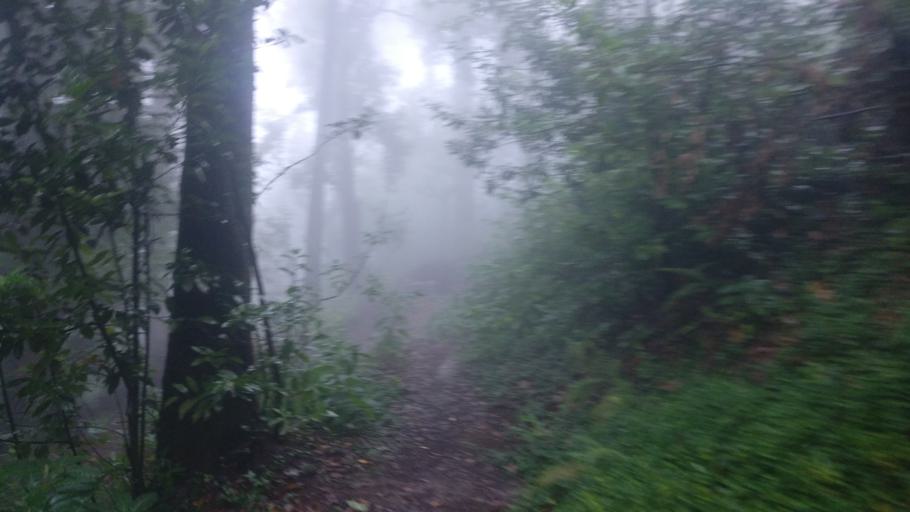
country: PT
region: Aveiro
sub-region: Mealhada
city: Pampilhosa do Botao
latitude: 40.3767
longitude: -8.3675
